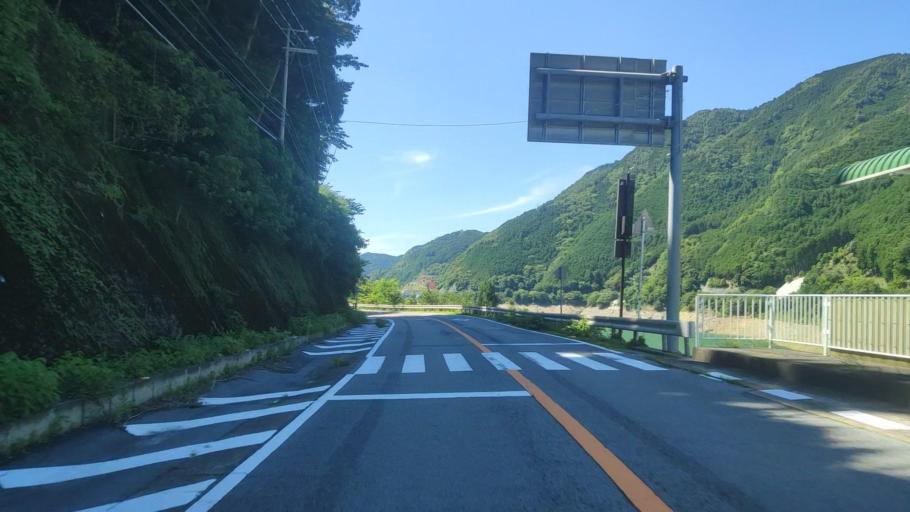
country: JP
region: Nara
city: Yoshino-cho
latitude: 34.3434
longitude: 135.9513
